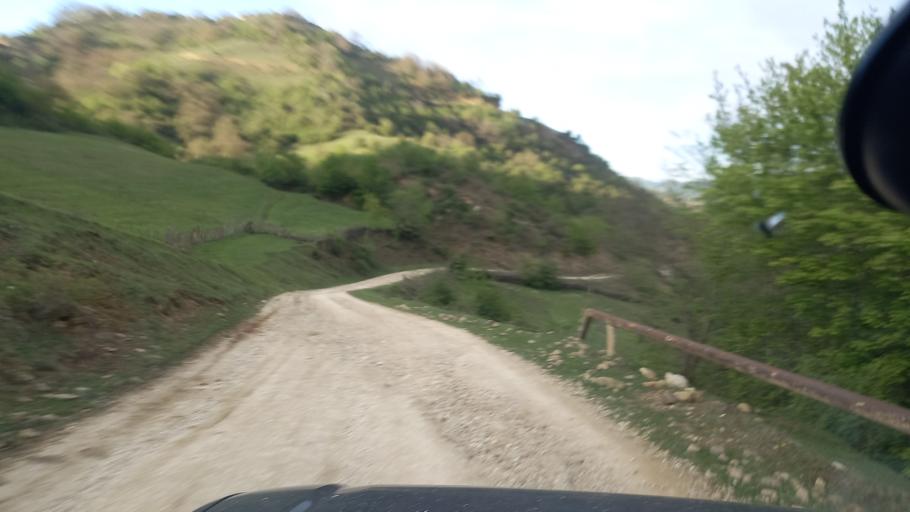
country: RU
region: Dagestan
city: Khuchni
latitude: 41.9496
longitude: 47.8384
